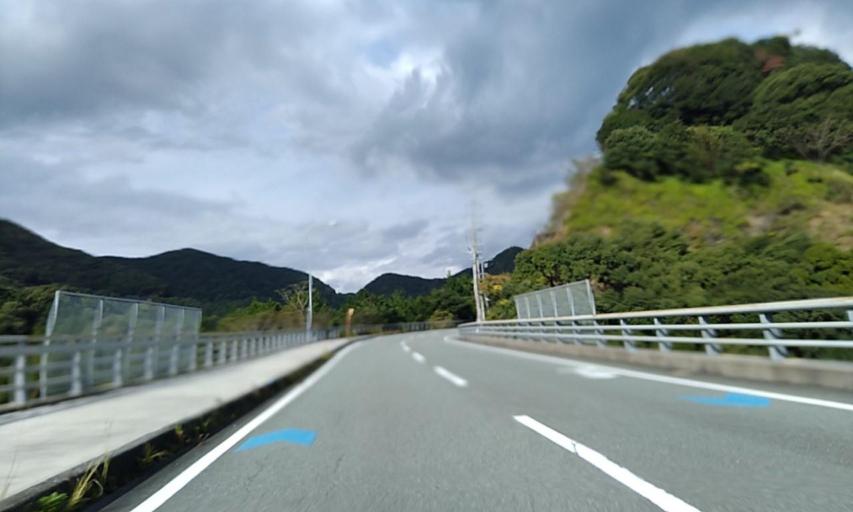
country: JP
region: Mie
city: Owase
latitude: 34.2460
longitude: 136.4019
